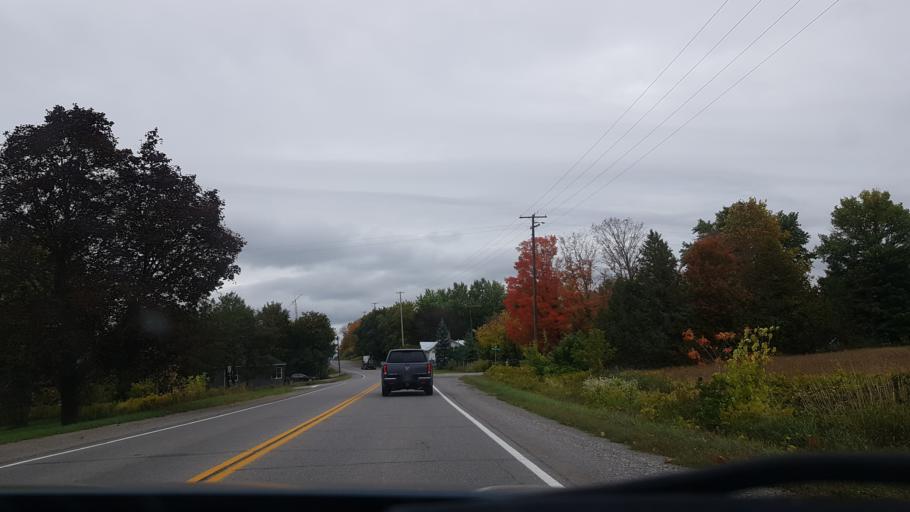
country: CA
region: Ontario
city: Omemee
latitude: 44.2247
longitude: -78.4795
